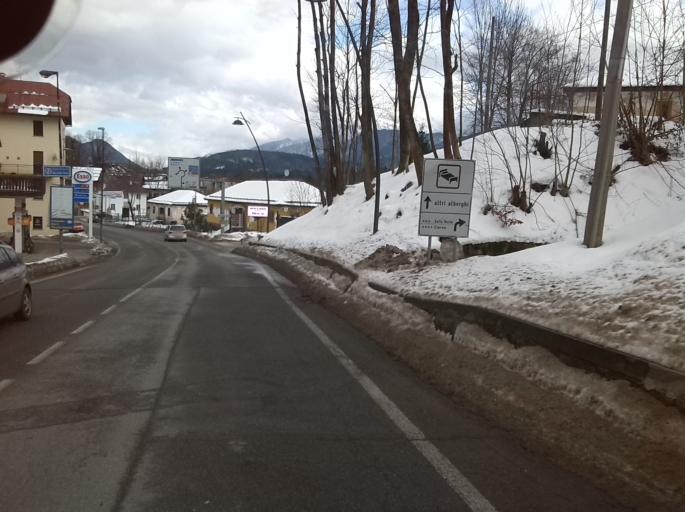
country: IT
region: Friuli Venezia Giulia
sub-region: Provincia di Udine
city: Tarvisio
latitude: 46.5056
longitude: 13.5687
